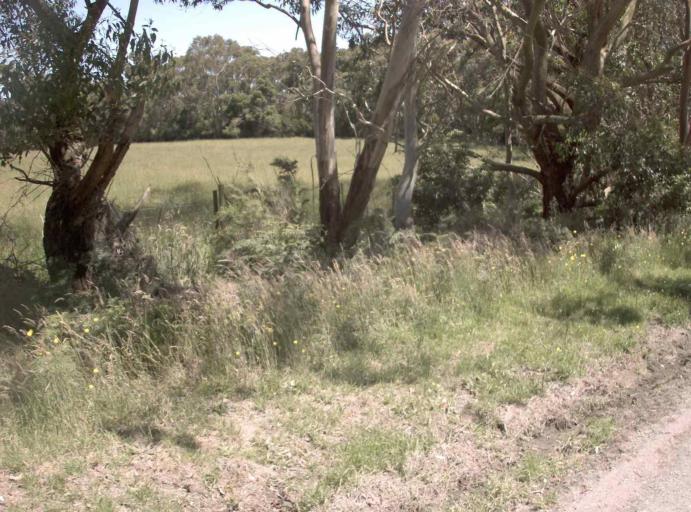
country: AU
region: Victoria
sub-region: Bass Coast
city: North Wonthaggi
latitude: -38.7653
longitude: 146.0631
